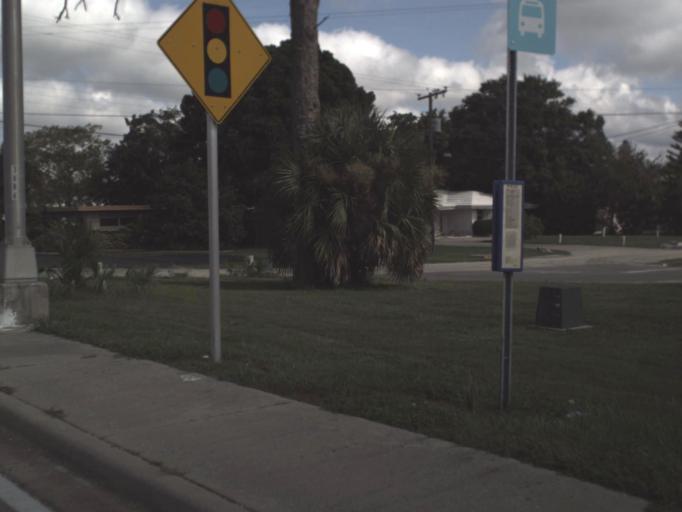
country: US
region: Florida
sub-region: Manatee County
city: Whitfield
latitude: 27.4155
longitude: -82.5740
